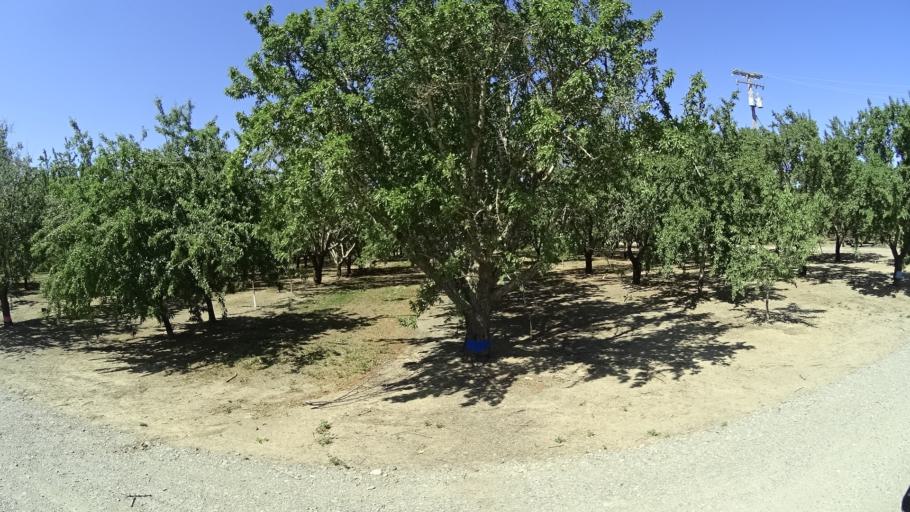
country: US
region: California
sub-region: Glenn County
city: Orland
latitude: 39.6852
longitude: -122.1592
